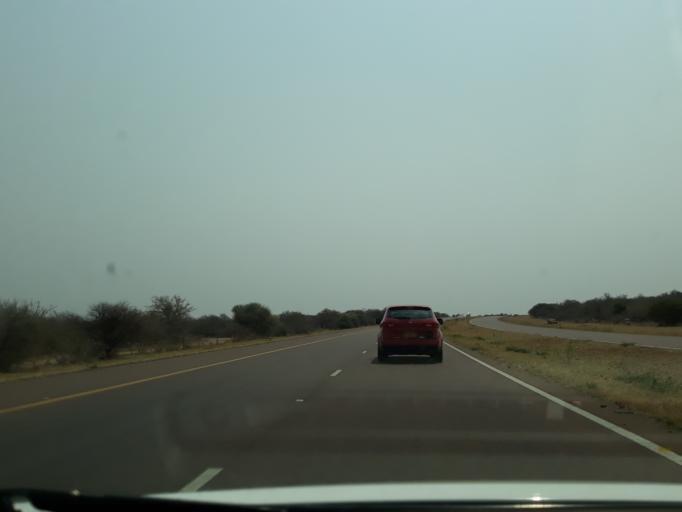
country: BW
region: Kgatleng
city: Bokaa
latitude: -24.4223
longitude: 26.0472
